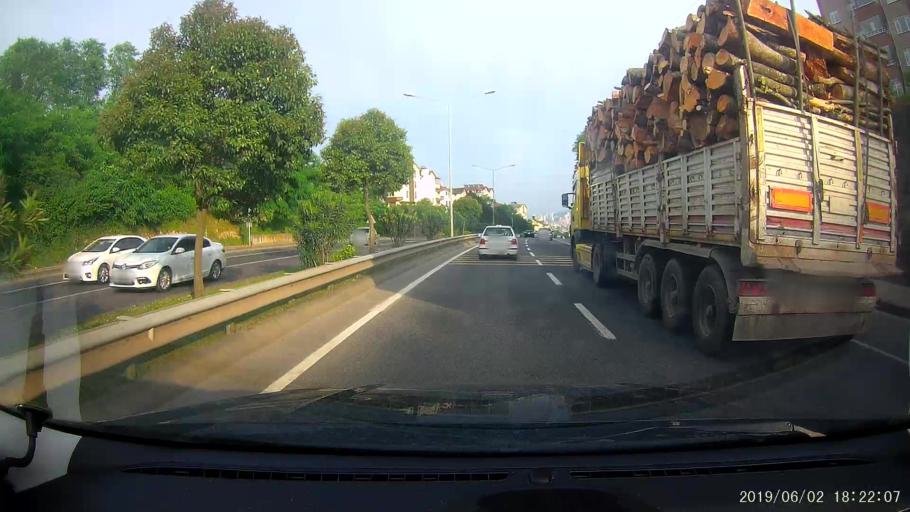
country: TR
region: Ordu
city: Fatsa
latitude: 41.0608
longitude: 37.4753
